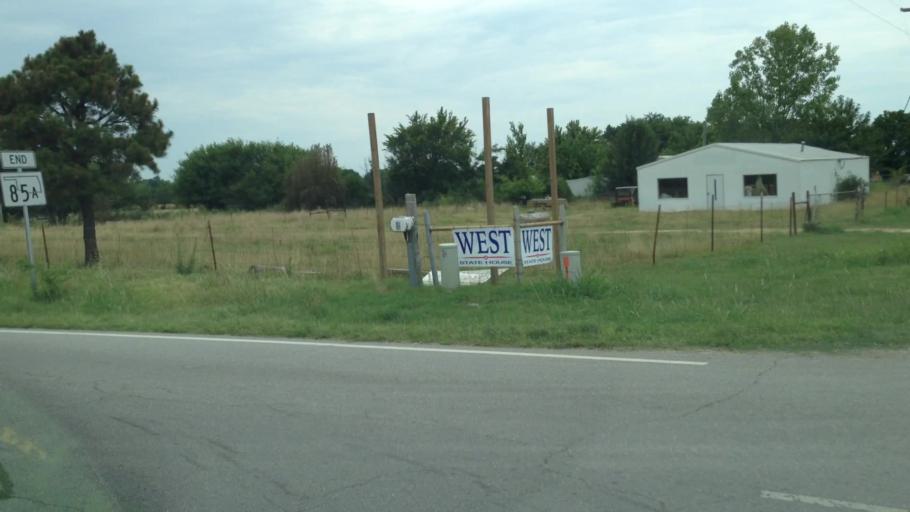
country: US
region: Oklahoma
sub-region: Delaware County
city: Cleora
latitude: 36.6125
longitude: -94.9634
